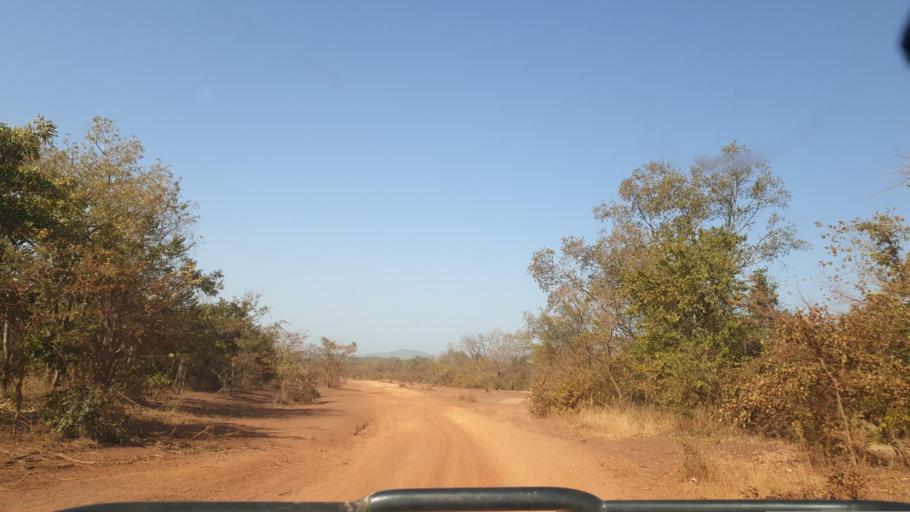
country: ML
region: Sikasso
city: Bougouni
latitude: 11.8209
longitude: -6.9591
